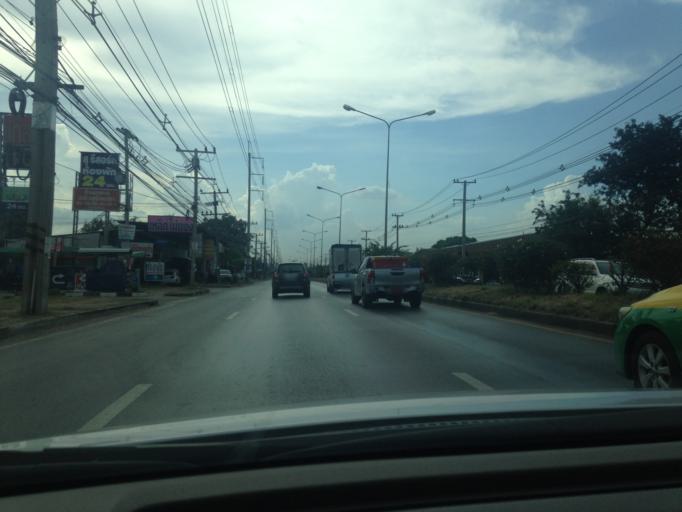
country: TH
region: Pathum Thani
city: Khlong Luang
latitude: 14.0666
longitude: 100.6826
